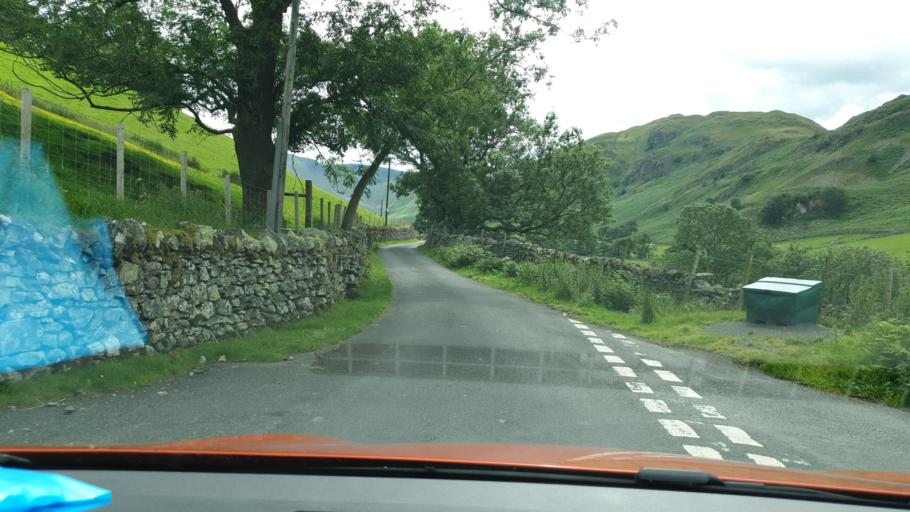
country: GB
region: England
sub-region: Cumbria
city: Ambleside
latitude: 54.5626
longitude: -2.8767
